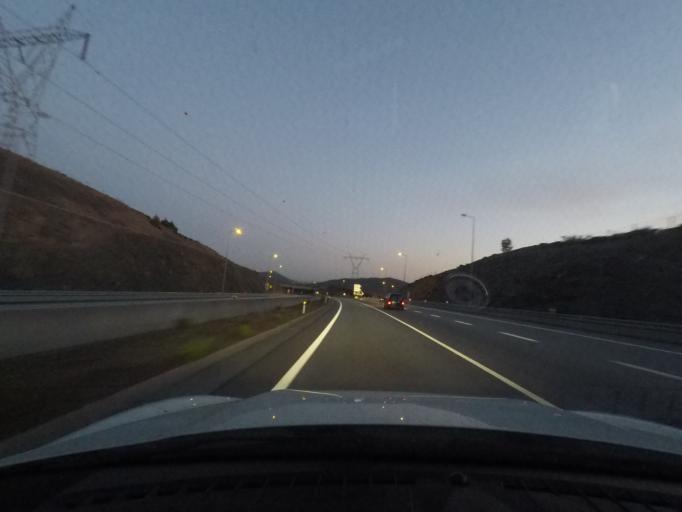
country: PT
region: Porto
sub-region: Valongo
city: Campo
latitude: 41.1670
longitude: -8.4493
